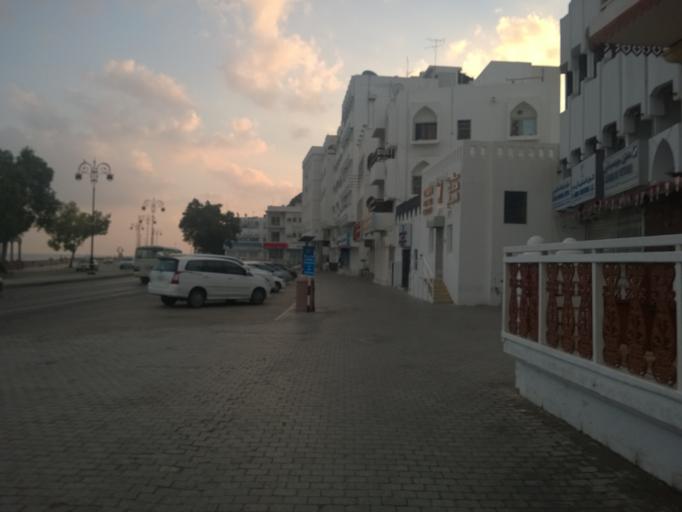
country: OM
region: Muhafazat Masqat
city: Muscat
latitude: 23.6204
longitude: 58.5651
